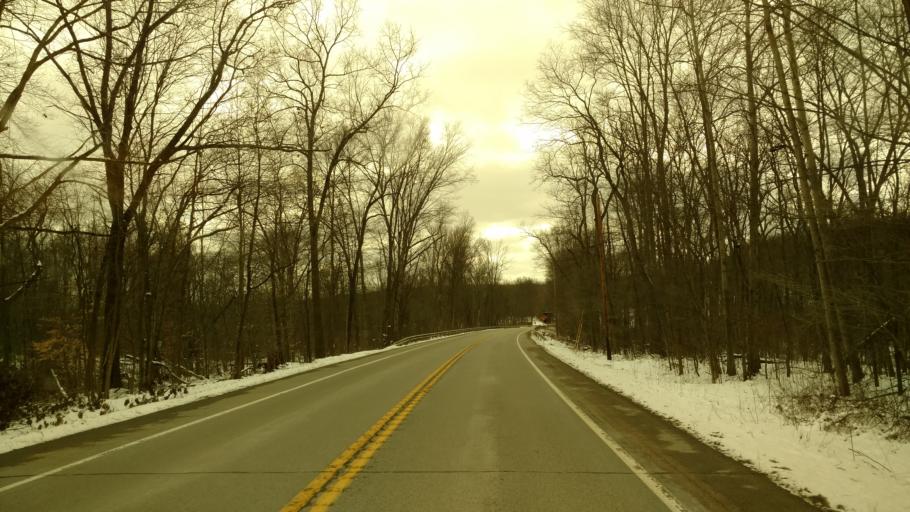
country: US
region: Pennsylvania
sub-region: Mercer County
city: Mercer
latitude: 41.3054
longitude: -80.2362
